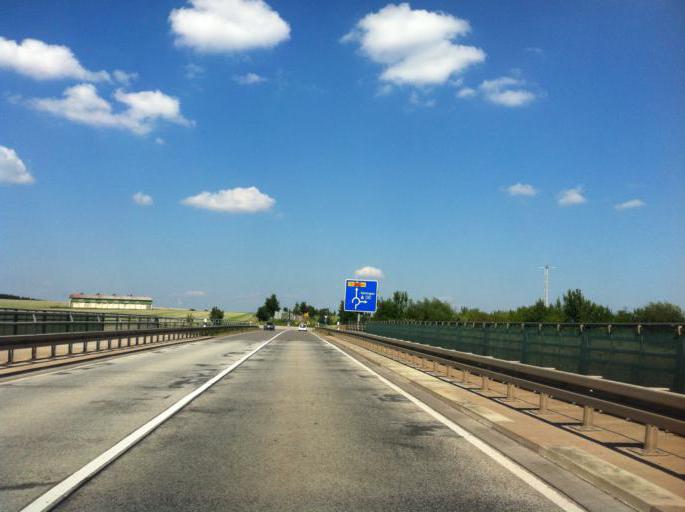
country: DE
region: Thuringia
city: Heilbad Heiligenstadt
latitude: 51.3969
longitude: 10.1298
